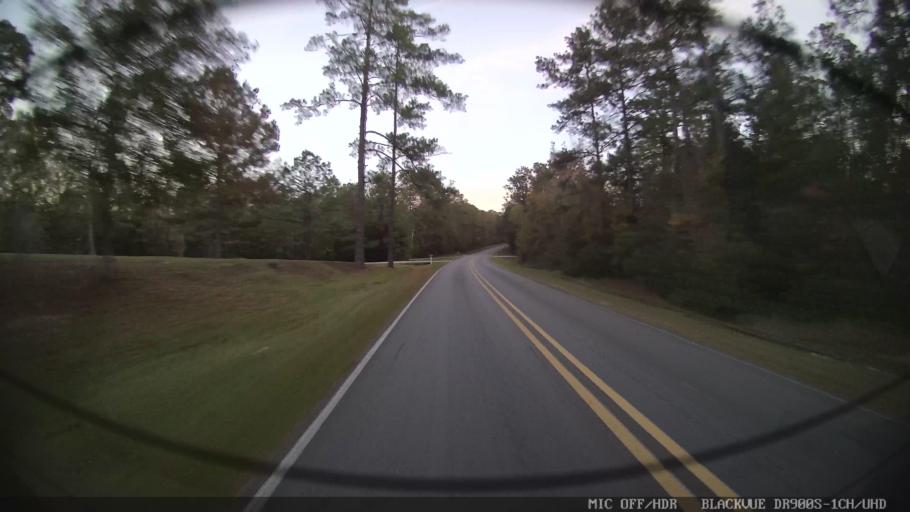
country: US
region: Mississippi
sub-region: Perry County
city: New Augusta
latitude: 31.0680
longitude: -89.1932
